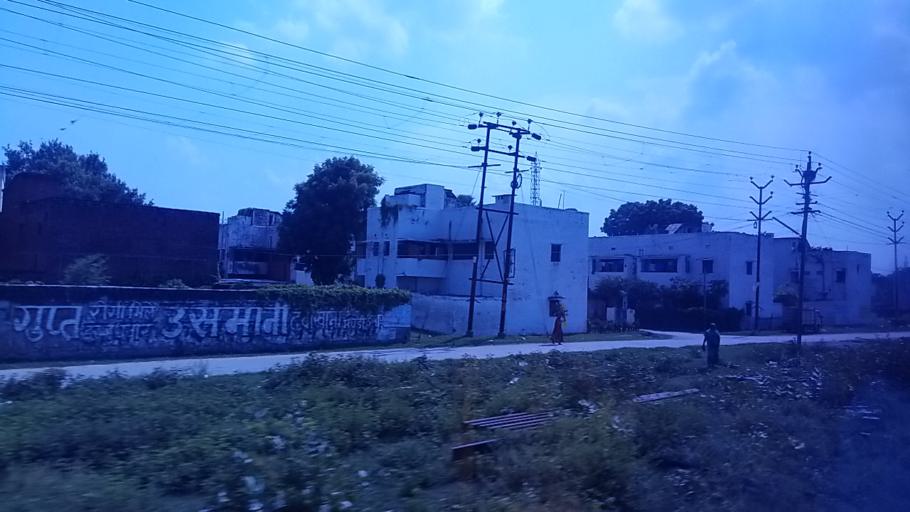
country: IN
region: Uttar Pradesh
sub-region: Allahabad
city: Allahabad
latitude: 25.4405
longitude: 81.7982
